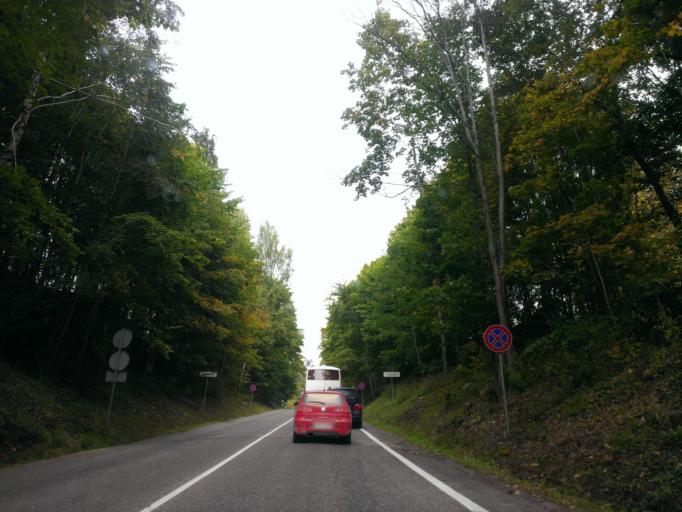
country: LV
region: Sigulda
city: Sigulda
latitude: 57.1851
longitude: 24.8471
